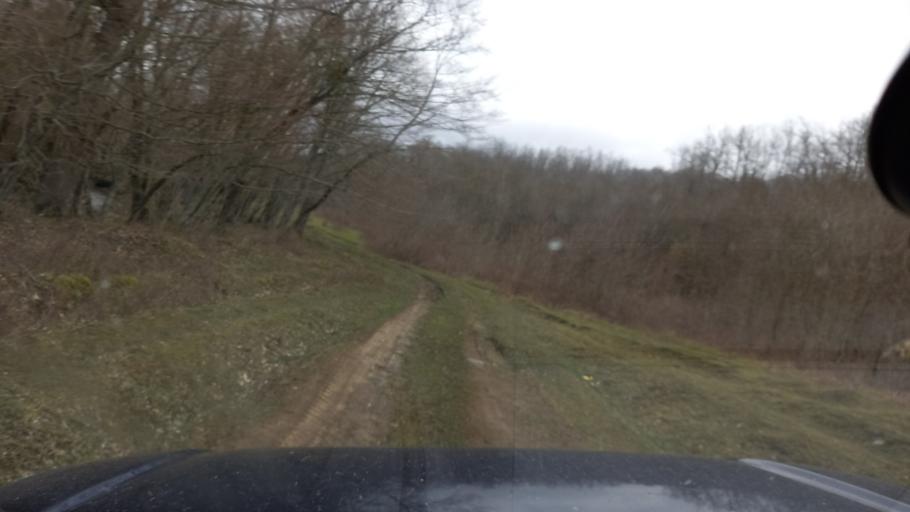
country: RU
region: Krasnodarskiy
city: Pshada
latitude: 44.4854
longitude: 38.3997
